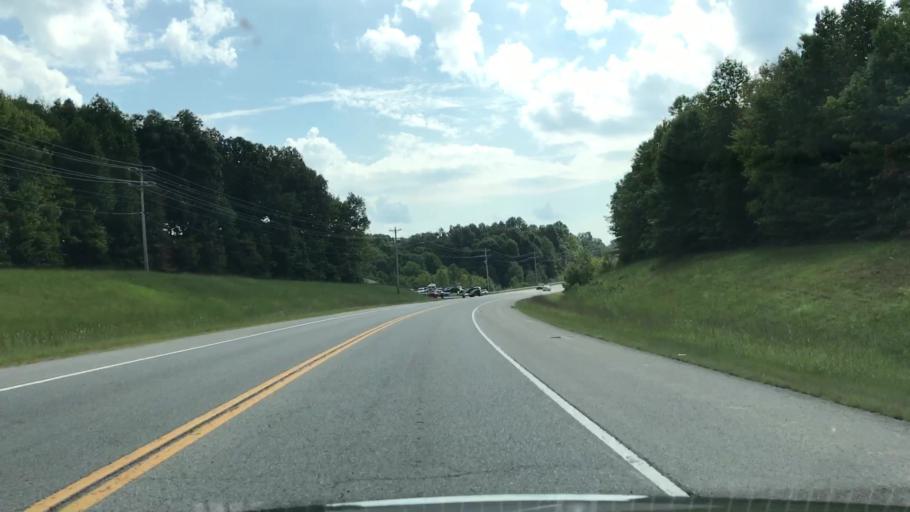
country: US
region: Tennessee
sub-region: Sumner County
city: Westmoreland
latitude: 36.5523
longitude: -86.2308
